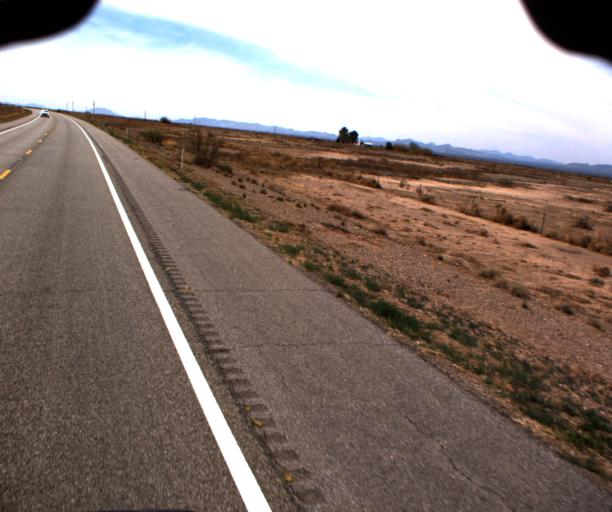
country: US
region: Arizona
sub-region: Cochise County
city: Pirtleville
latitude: 31.5594
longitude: -109.6665
